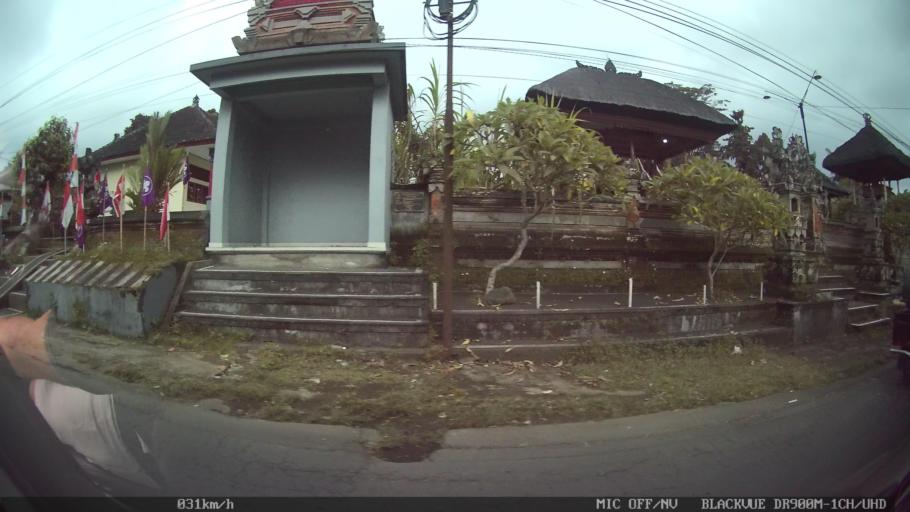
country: ID
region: Bali
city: Banjar Triwangsakeliki
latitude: -8.4502
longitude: 115.2622
